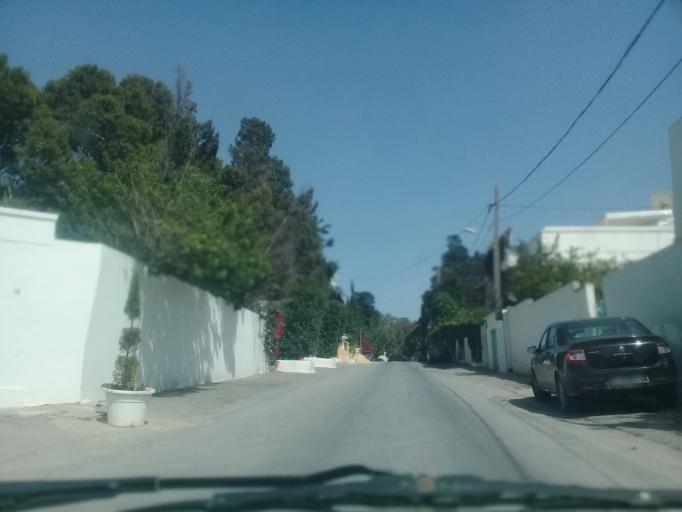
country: TN
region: Tunis
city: Al Marsa
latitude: 36.8813
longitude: 10.3371
